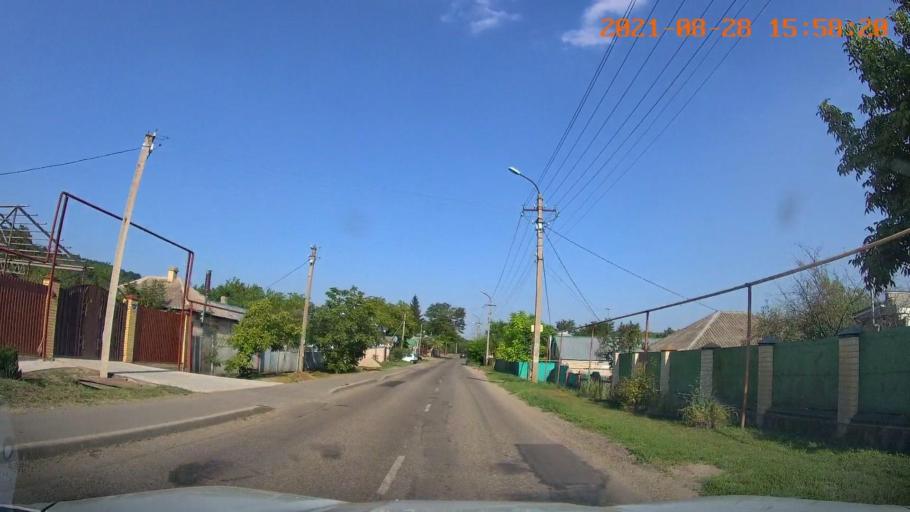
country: RU
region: Stavropol'skiy
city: Tatarka
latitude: 44.9611
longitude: 41.9504
